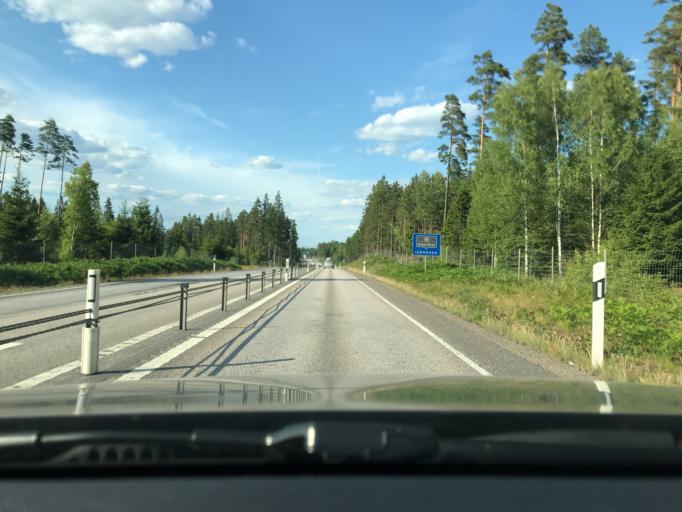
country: SE
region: Kronoberg
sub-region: Vaxjo Kommun
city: Braas
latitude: 57.0097
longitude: 15.0463
